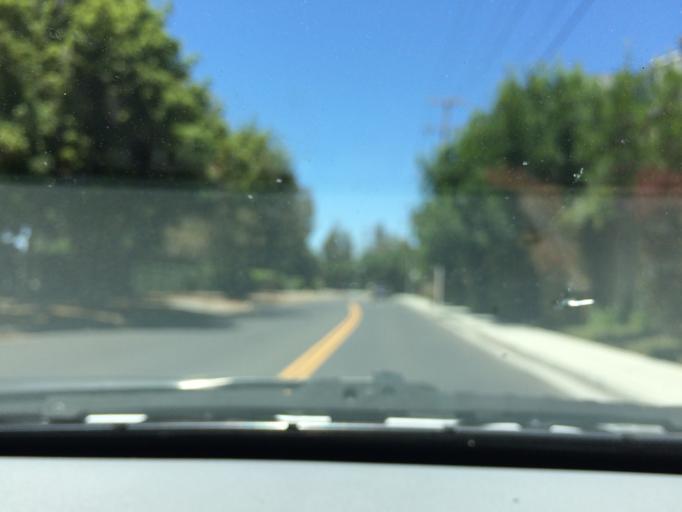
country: US
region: California
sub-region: San Mateo County
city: East Palo Alto
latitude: 37.4674
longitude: -122.1566
